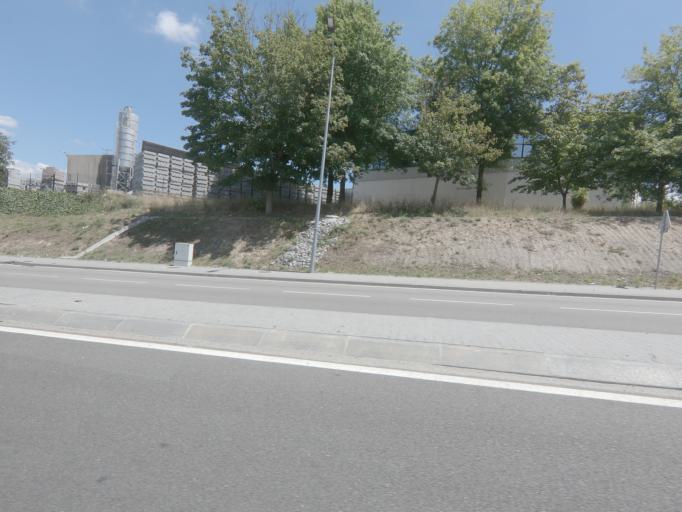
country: PT
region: Porto
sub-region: Paredes
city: Paredes
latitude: 41.1983
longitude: -8.3080
